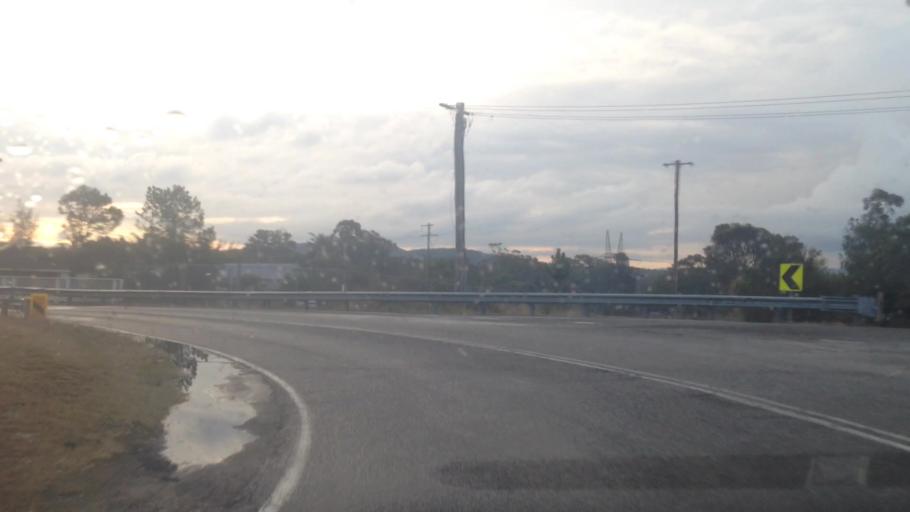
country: AU
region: New South Wales
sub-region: Wyong Shire
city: Charmhaven
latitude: -33.1759
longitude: 151.4872
